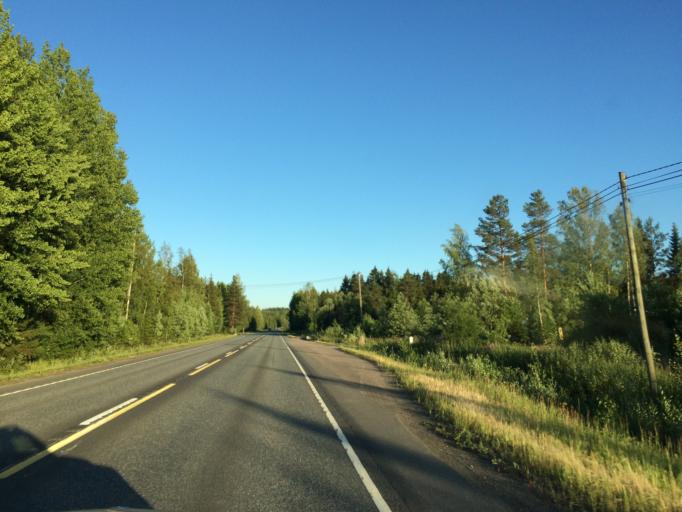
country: FI
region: Haeme
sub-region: Haemeenlinna
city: Tervakoski
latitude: 60.7762
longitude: 24.6962
